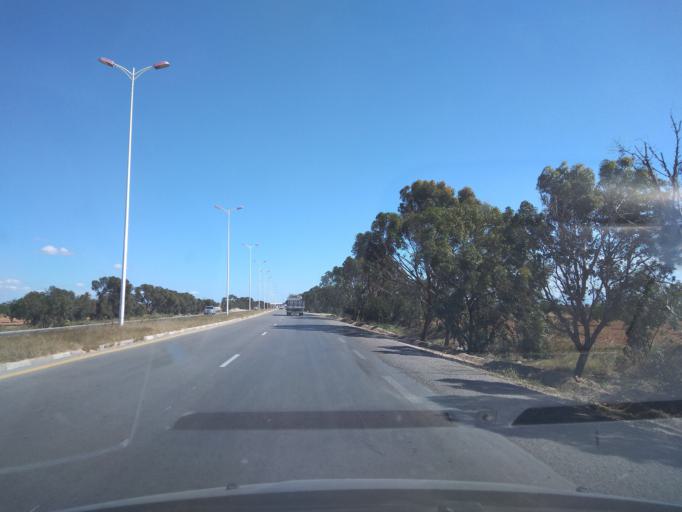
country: TN
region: Safaqis
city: Sfax
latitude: 34.8238
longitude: 10.7138
